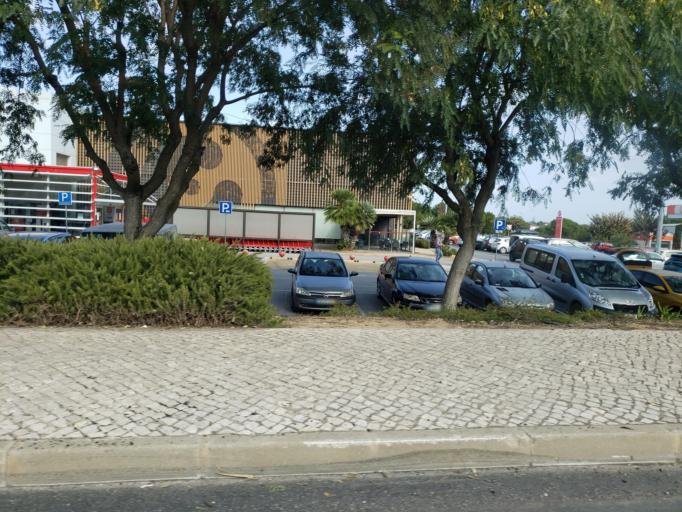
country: PT
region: Faro
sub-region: Portimao
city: Portimao
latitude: 37.1512
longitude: -8.5528
